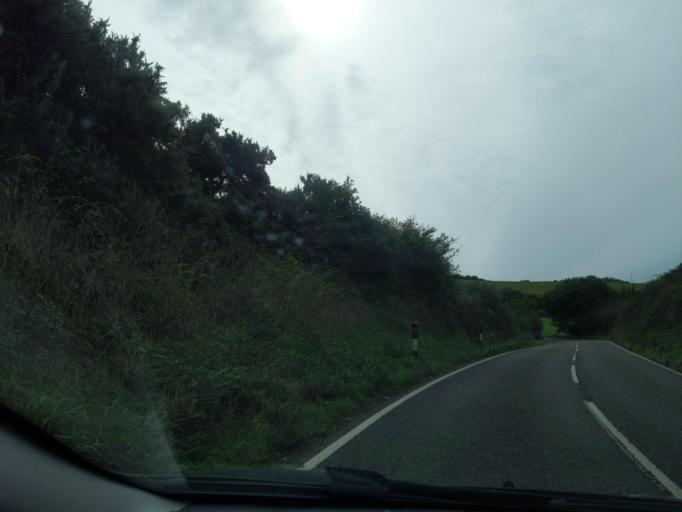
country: GB
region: England
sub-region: Cornwall
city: Mevagissey
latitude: 50.2872
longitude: -4.7865
